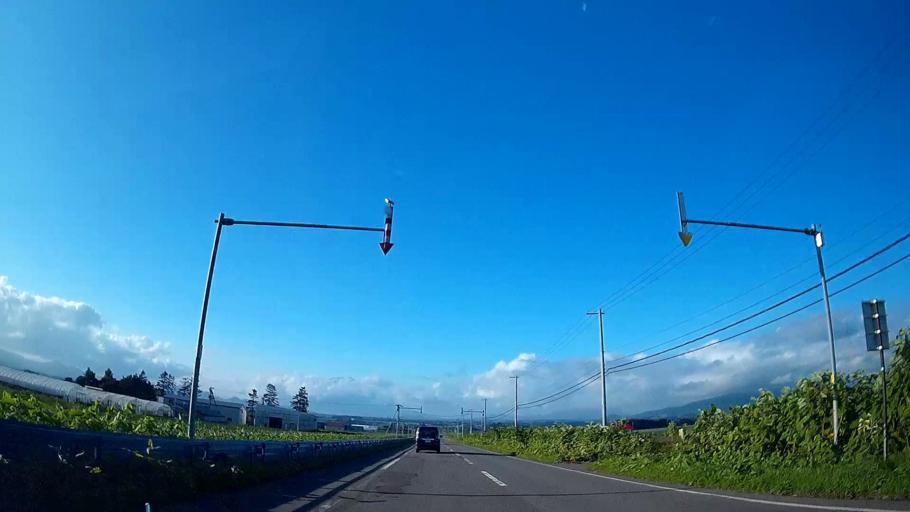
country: JP
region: Hokkaido
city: Date
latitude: 42.6294
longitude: 140.7998
